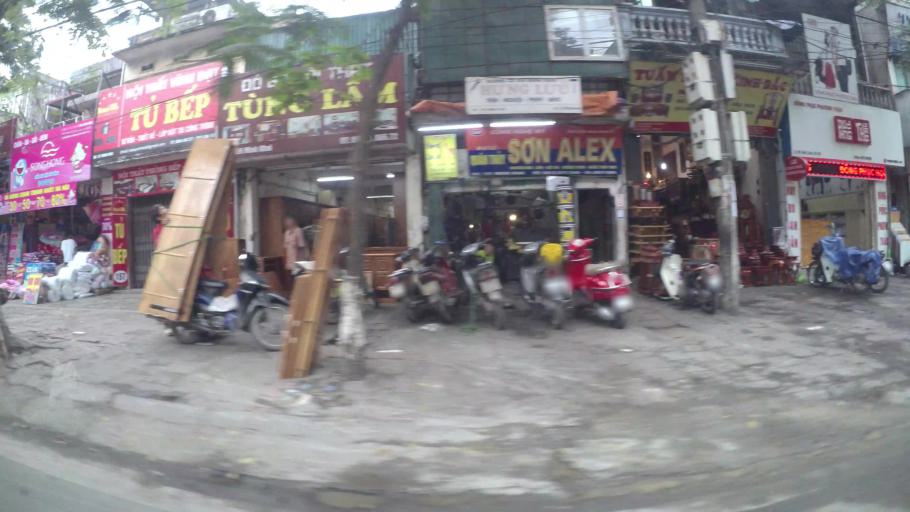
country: VN
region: Ha Noi
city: Hai BaTrung
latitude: 20.9953
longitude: 105.8554
